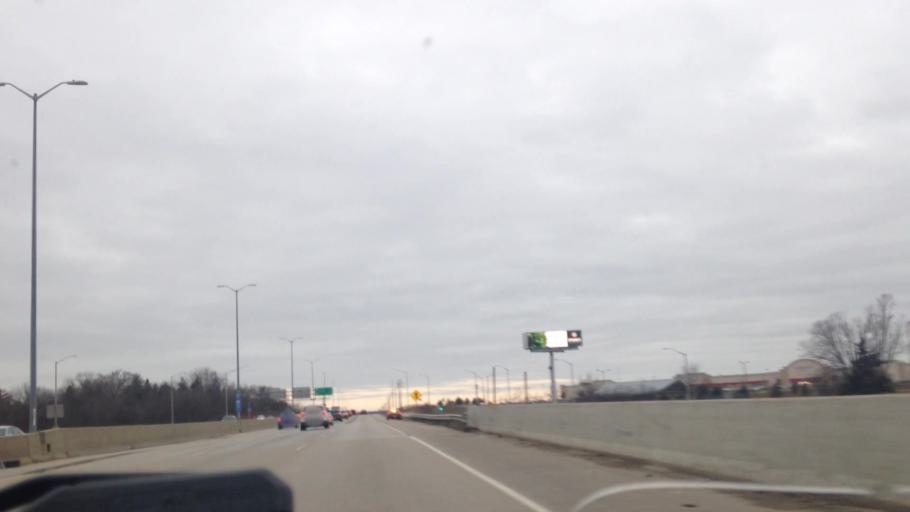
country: US
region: Wisconsin
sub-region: Waukesha County
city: Butler
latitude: 43.1604
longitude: -88.0643
